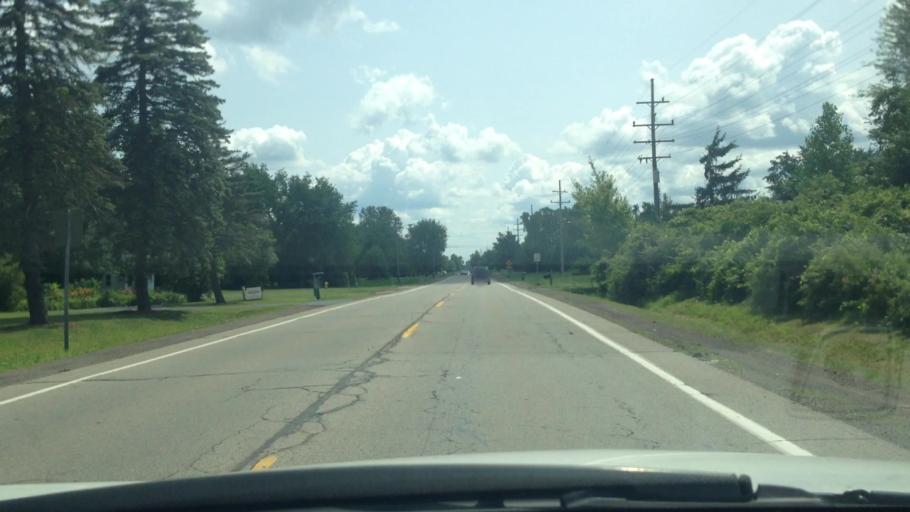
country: US
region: Michigan
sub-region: Wayne County
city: Flat Rock
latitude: 42.1623
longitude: -83.3056
